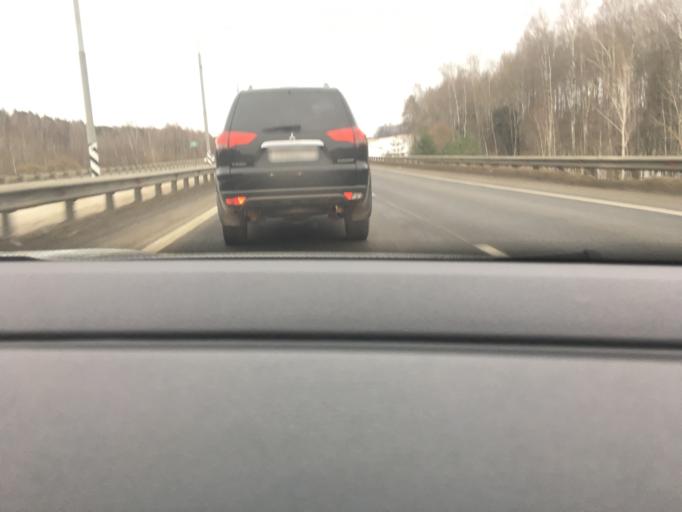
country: RU
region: Tula
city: Zaokskiy
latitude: 54.8191
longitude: 37.4756
